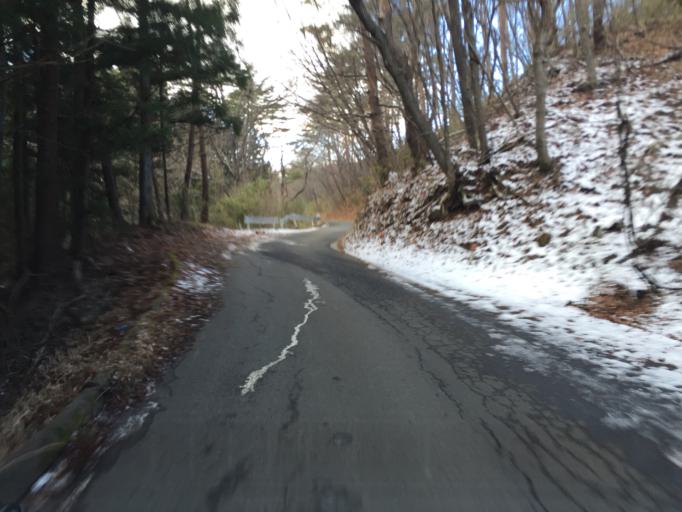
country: JP
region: Fukushima
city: Nihommatsu
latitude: 37.6745
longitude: 140.3711
